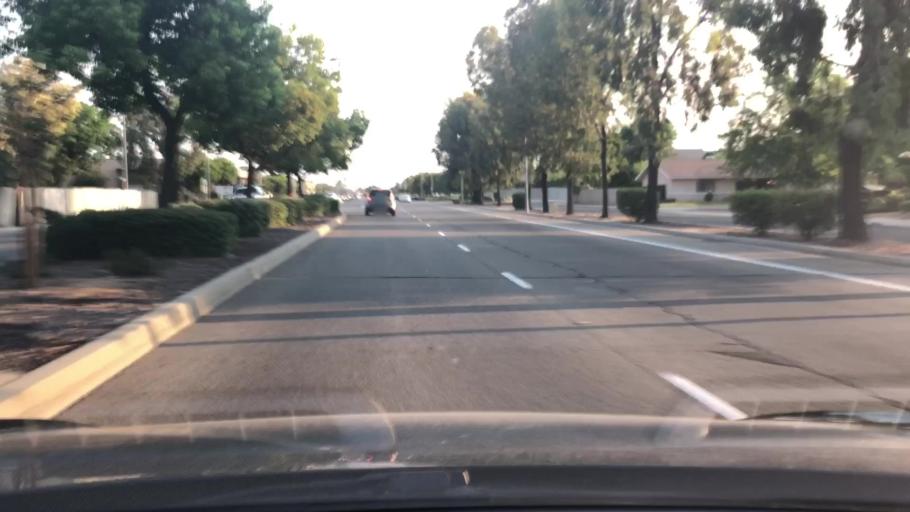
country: US
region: California
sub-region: Fresno County
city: Clovis
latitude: 36.8331
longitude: -119.7294
